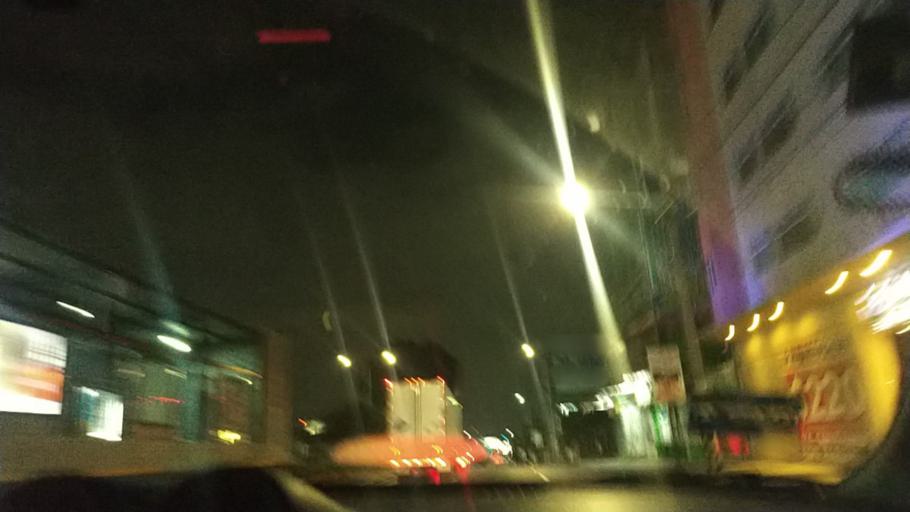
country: MX
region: Mexico
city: Ecatepec
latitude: 19.6187
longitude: -99.0672
